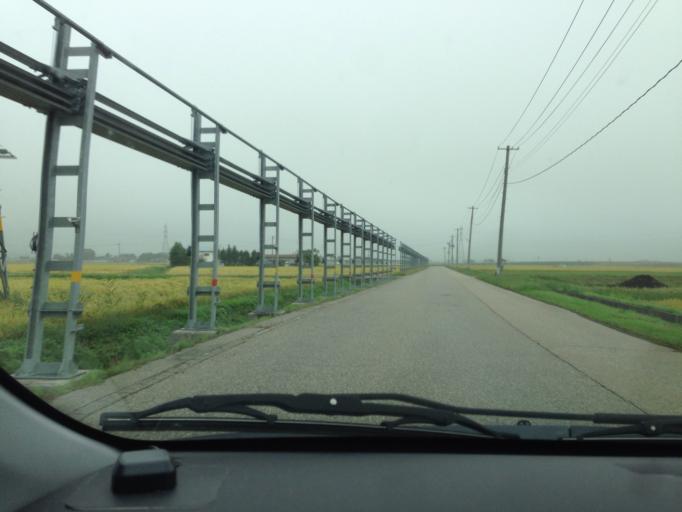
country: JP
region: Fukushima
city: Kitakata
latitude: 37.5743
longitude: 139.8537
